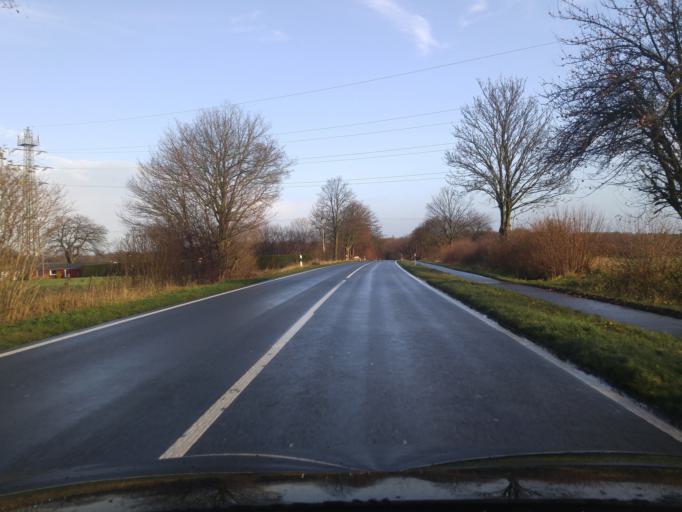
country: DE
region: Schleswig-Holstein
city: Ratekau
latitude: 53.9541
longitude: 10.7539
